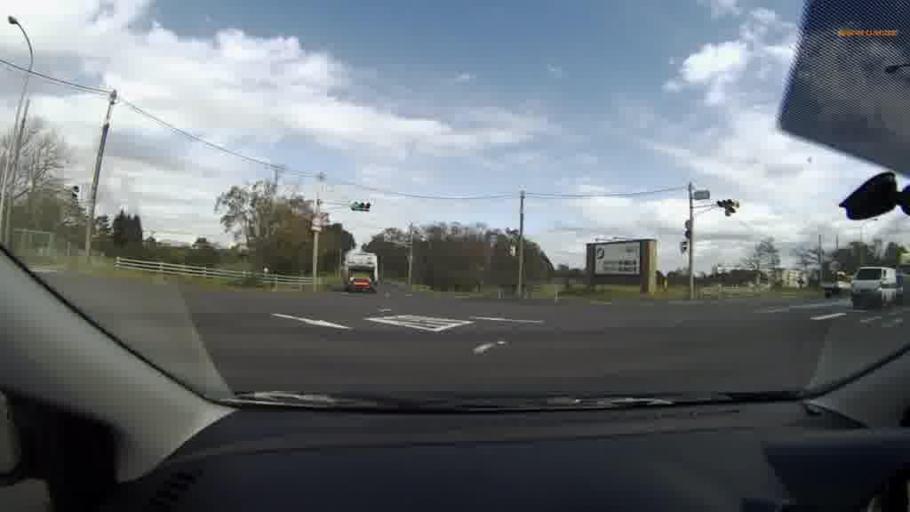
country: JP
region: Hokkaido
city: Kushiro
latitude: 43.0100
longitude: 144.2873
